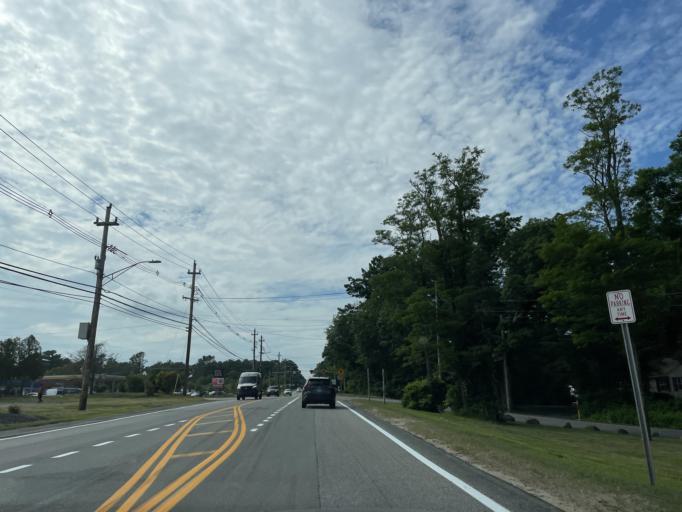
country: US
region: Rhode Island
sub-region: Kent County
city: West Greenwich
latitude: 41.6081
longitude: -71.6622
